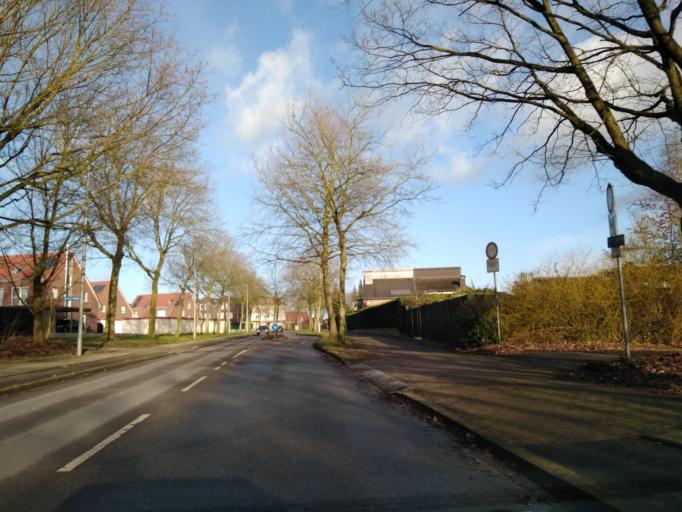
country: DE
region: North Rhine-Westphalia
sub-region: Regierungsbezirk Munster
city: Gladbeck
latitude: 51.5865
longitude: 6.9576
